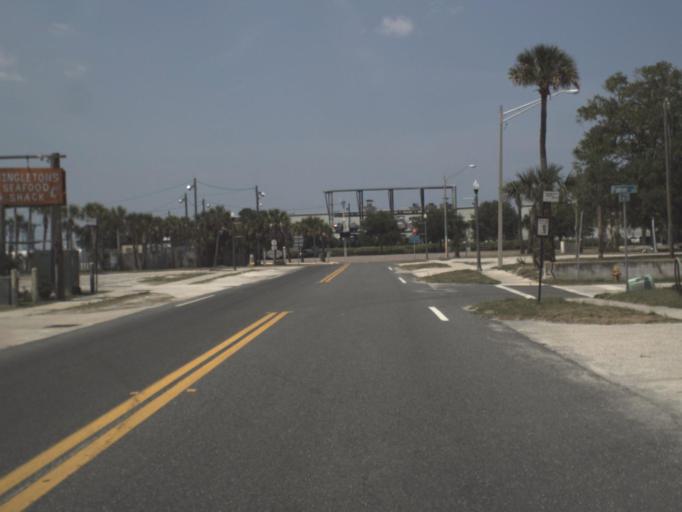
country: US
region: Florida
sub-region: Duval County
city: Atlantic Beach
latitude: 30.3942
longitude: -81.4301
